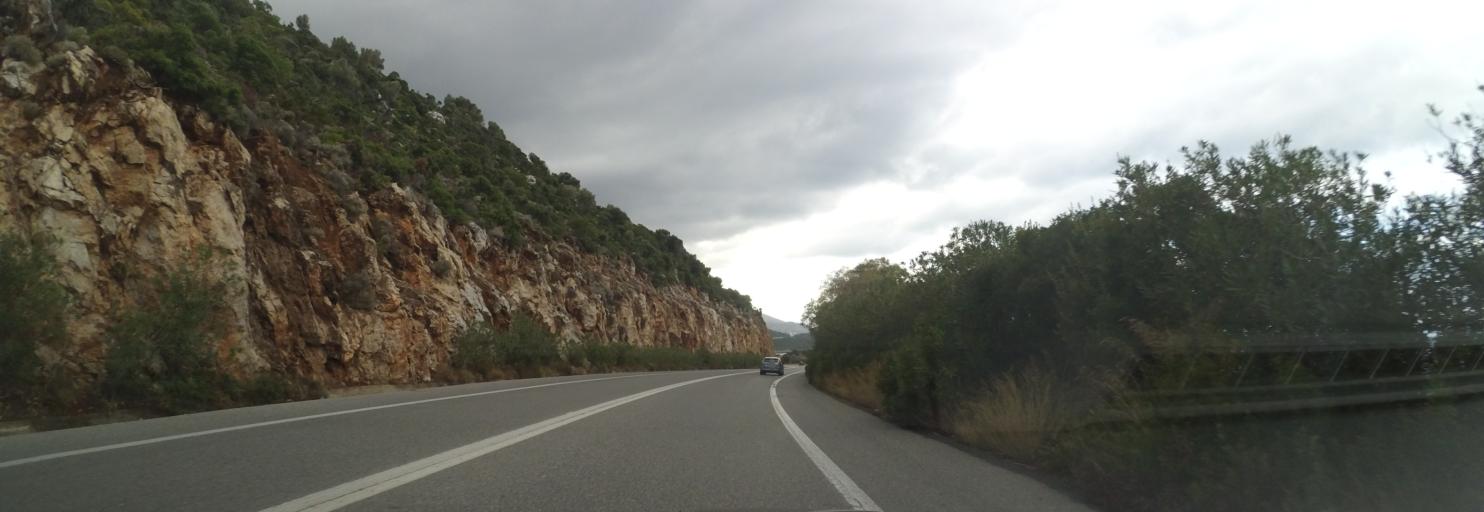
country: GR
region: Crete
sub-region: Nomos Rethymnis
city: Zoniana
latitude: 35.4050
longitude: 24.8526
